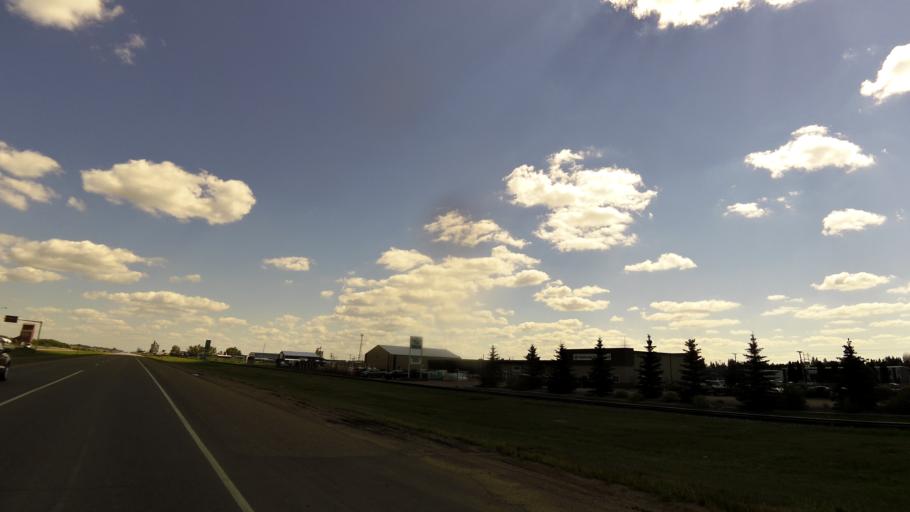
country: CA
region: Saskatchewan
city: North Battleford
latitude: 52.7539
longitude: -108.2645
